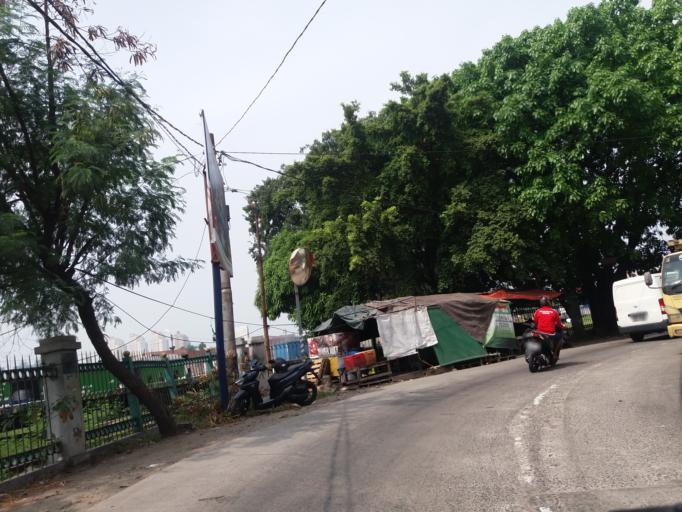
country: ID
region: Jakarta Raya
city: Jakarta
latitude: -6.1326
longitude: 106.8170
